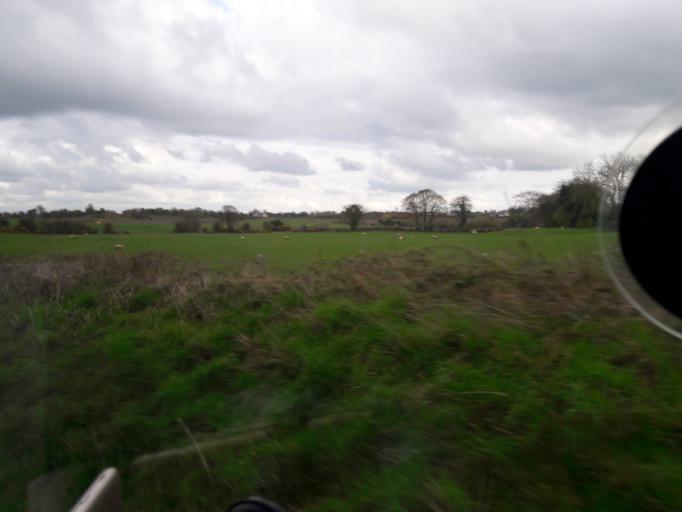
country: IE
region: Leinster
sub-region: An Iarmhi
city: Rathwire
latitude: 53.4921
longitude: -7.1961
